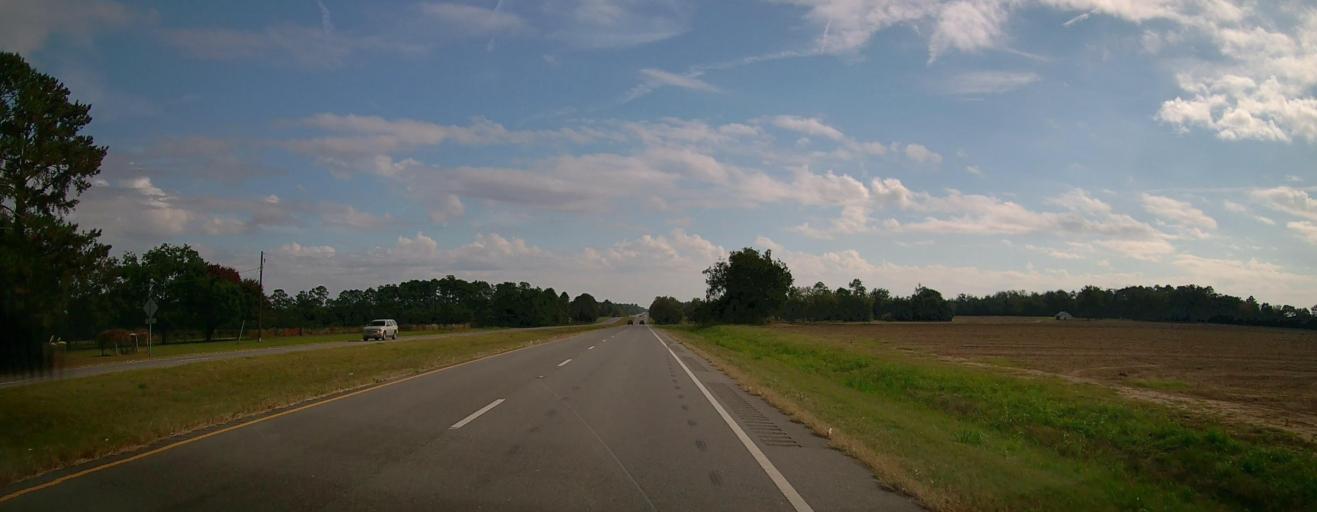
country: US
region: Georgia
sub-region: Thomas County
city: Meigs
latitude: 31.0297
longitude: -84.0622
